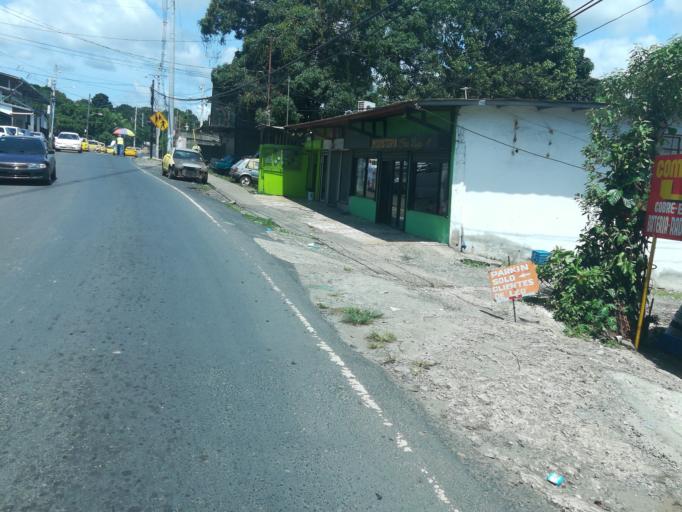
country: PA
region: Panama
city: Tocumen
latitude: 9.0819
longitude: -79.4047
